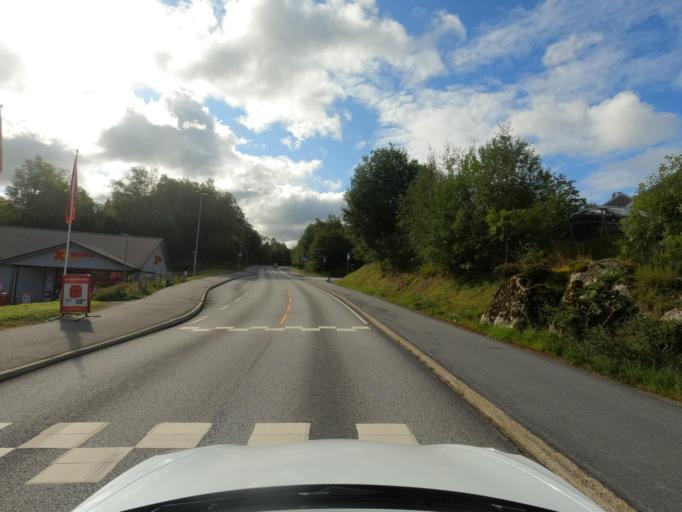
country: NO
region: Hordaland
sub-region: Bergen
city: Espeland
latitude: 60.3451
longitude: 5.3934
